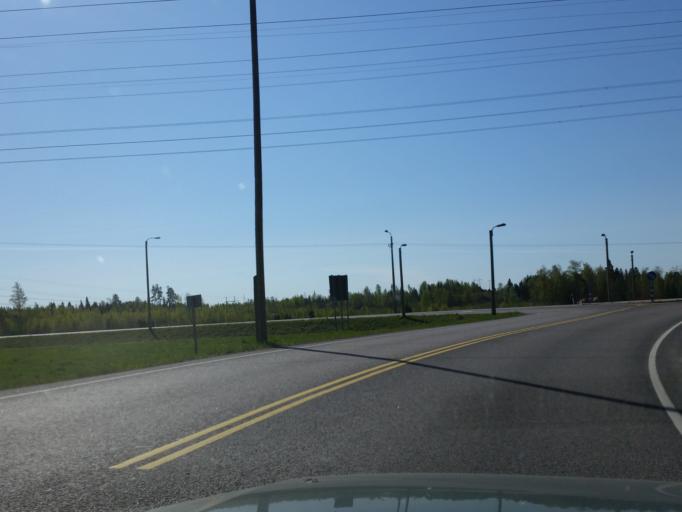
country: FI
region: Uusimaa
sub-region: Helsinki
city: Lohja
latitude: 60.1792
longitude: 23.9921
